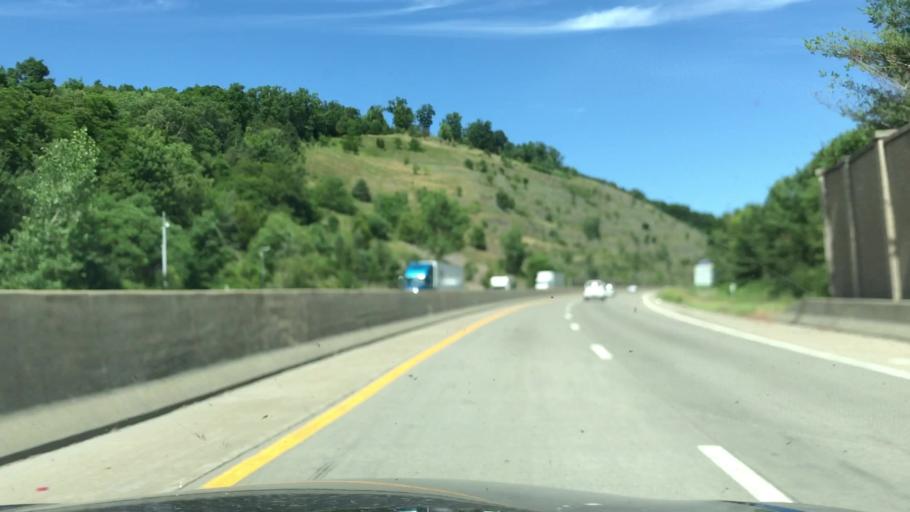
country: US
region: New York
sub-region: Steuben County
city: Corning
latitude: 42.1628
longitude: -77.0693
